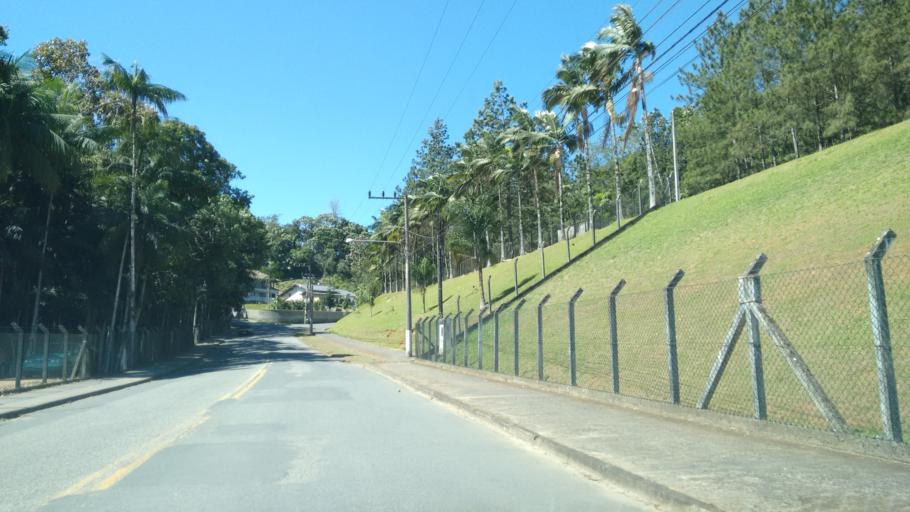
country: BR
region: Santa Catarina
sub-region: Blumenau
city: Blumenau
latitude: -26.8855
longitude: -49.1384
